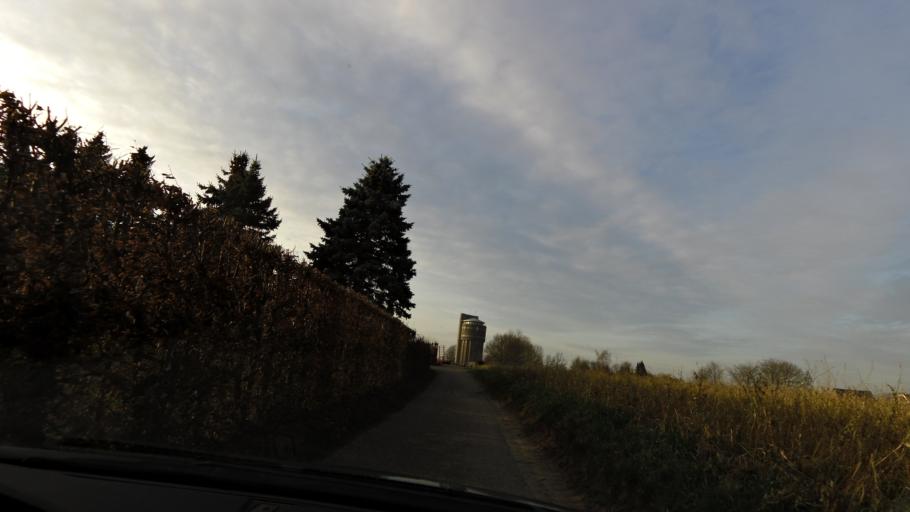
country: NL
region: Limburg
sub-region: Valkenburg aan de Geul
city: Broekhem
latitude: 50.9005
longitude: 5.8260
